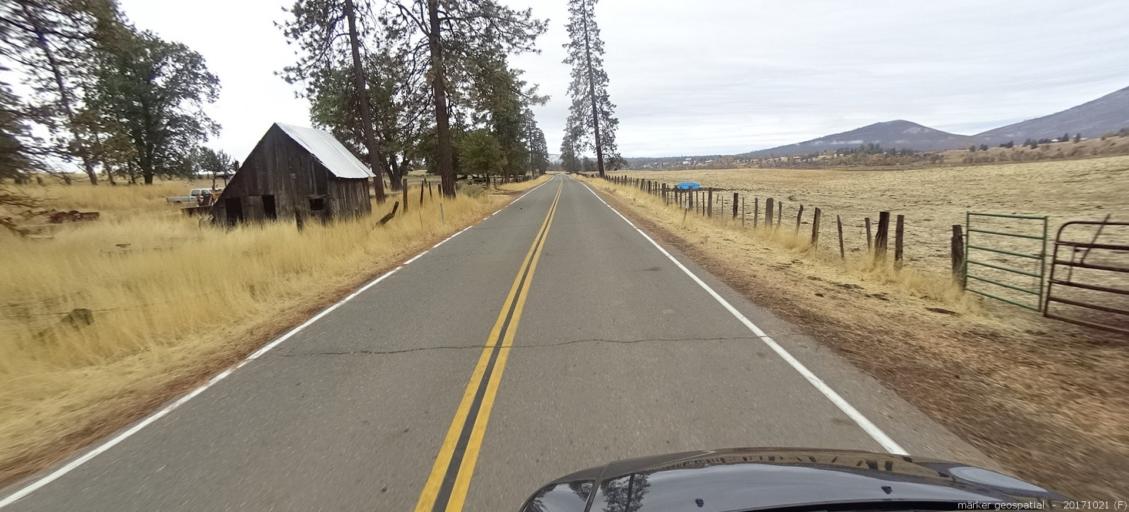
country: US
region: California
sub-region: Shasta County
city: Burney
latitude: 41.0178
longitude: -121.4134
